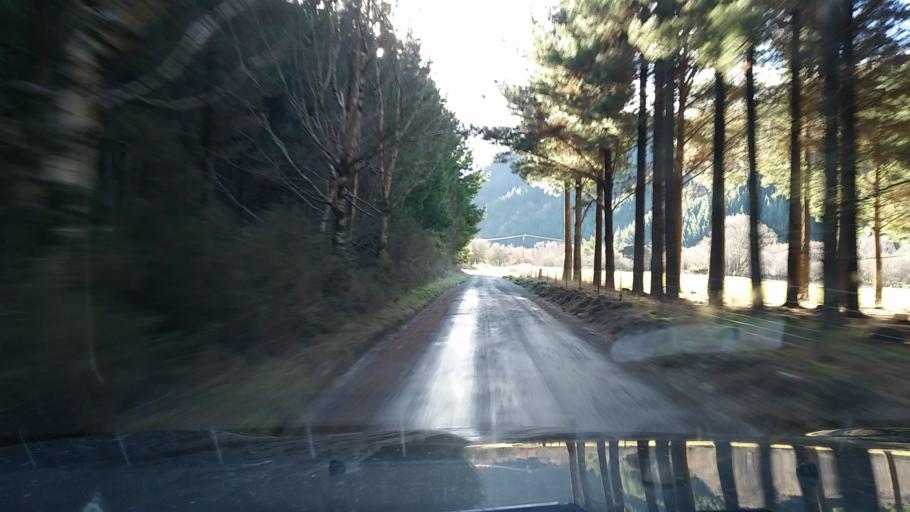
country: NZ
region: Nelson
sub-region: Nelson City
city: Nelson
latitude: -41.5526
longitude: 173.4229
